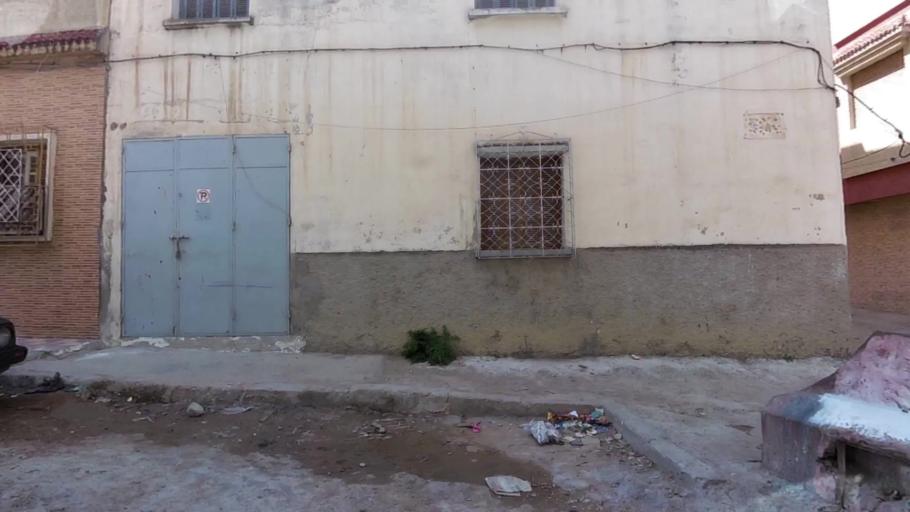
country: MA
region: Tanger-Tetouan
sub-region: Tanger-Assilah
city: Tangier
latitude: 35.7565
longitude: -5.8054
